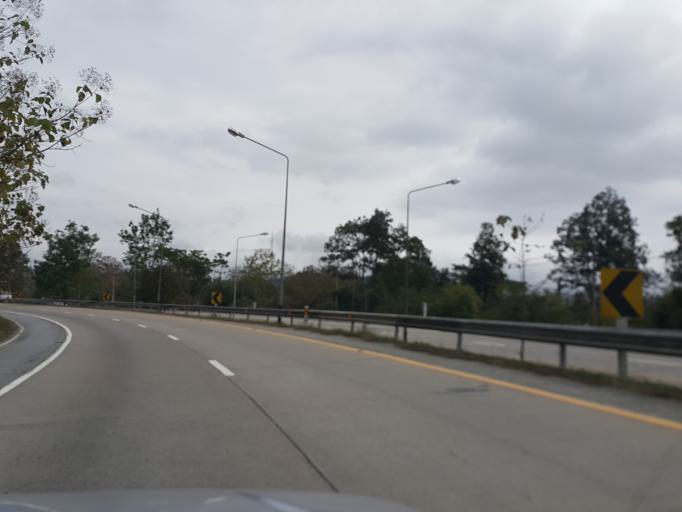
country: TH
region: Lamphun
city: Mae Tha
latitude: 18.4626
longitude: 99.1325
